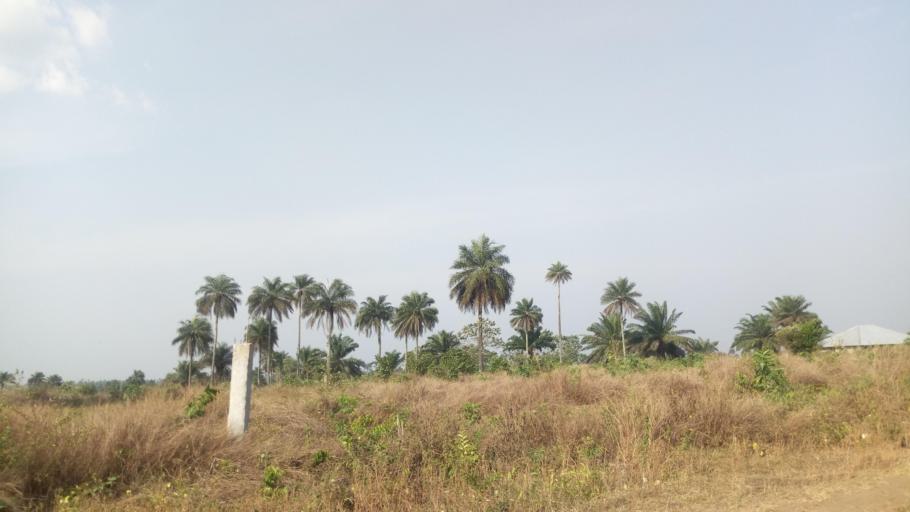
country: SL
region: Southern Province
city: Mogbwemo
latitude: 7.6150
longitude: -12.1749
